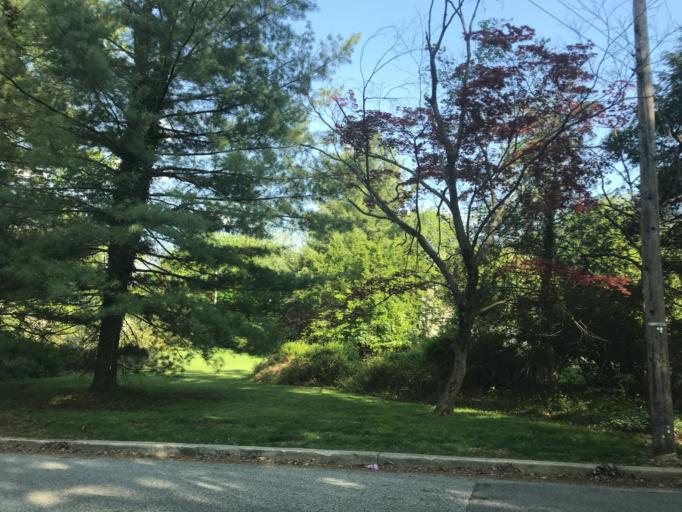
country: US
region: Maryland
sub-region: Baltimore County
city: Lutherville
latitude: 39.3707
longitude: -76.6611
